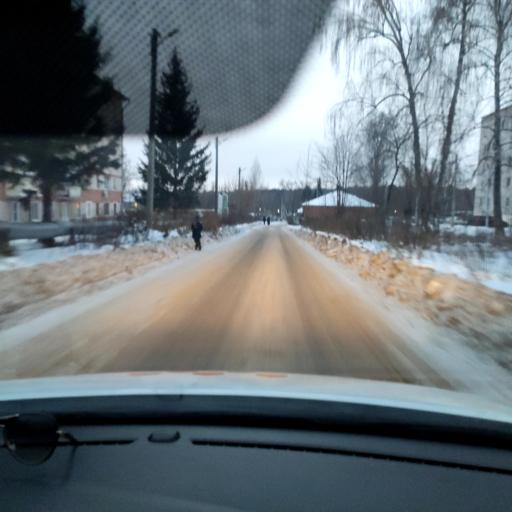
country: RU
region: Tatarstan
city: Vysokaya Gora
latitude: 55.9281
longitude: 49.2025
